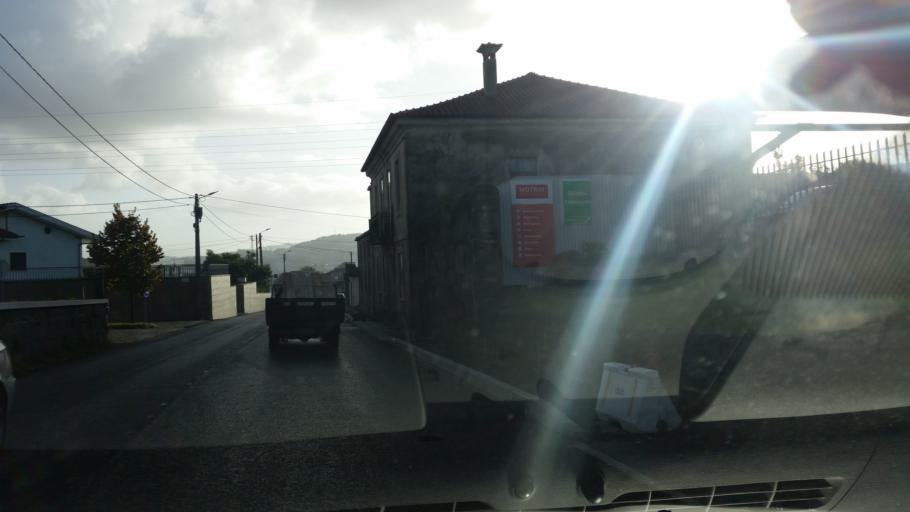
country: PT
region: Porto
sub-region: Santo Tirso
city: Aves
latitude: 41.3583
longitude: -8.4385
